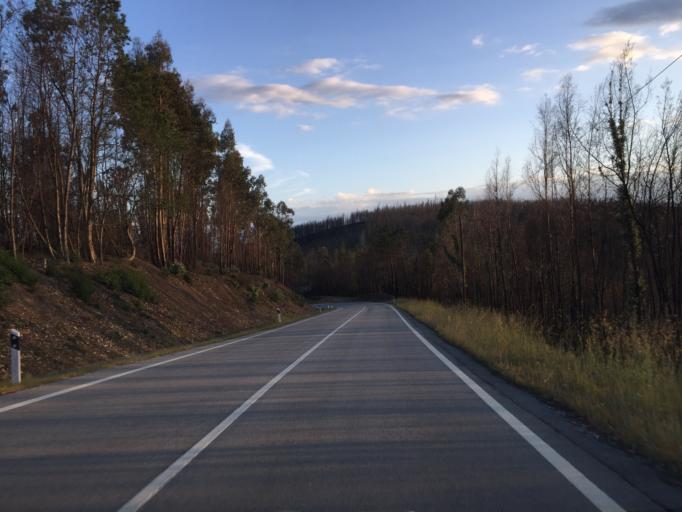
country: PT
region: Coimbra
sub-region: Pampilhosa da Serra
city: Pampilhosa da Serra
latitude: 40.0701
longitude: -7.9745
